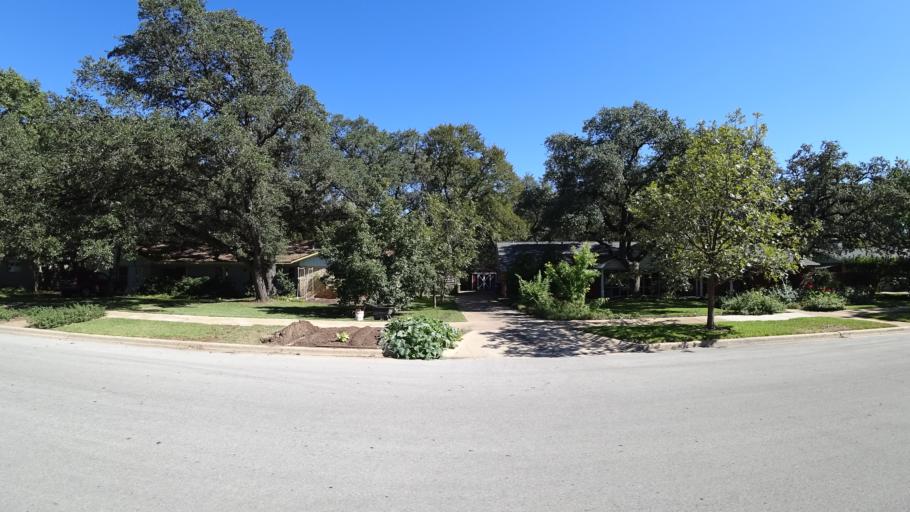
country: US
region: Texas
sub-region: Travis County
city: West Lake Hills
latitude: 30.3382
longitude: -97.7489
